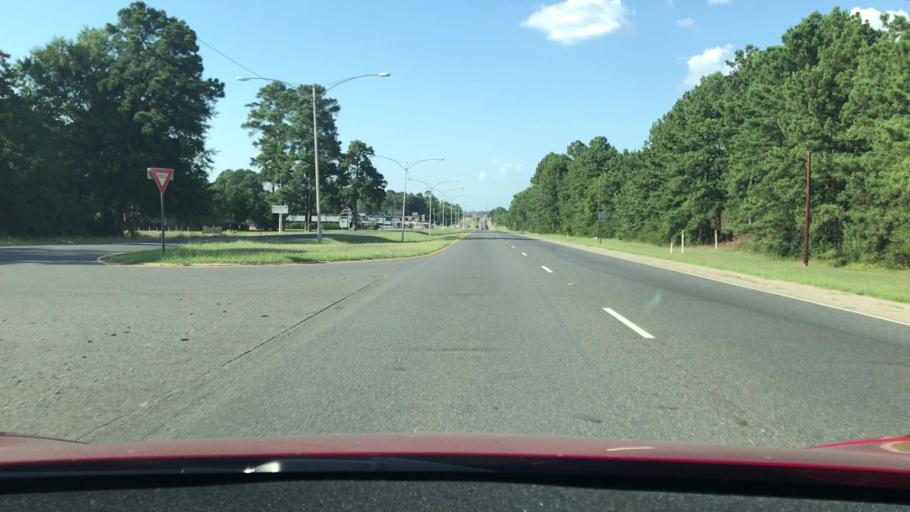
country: US
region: Louisiana
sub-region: Bossier Parish
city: Bossier City
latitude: 32.4219
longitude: -93.7870
